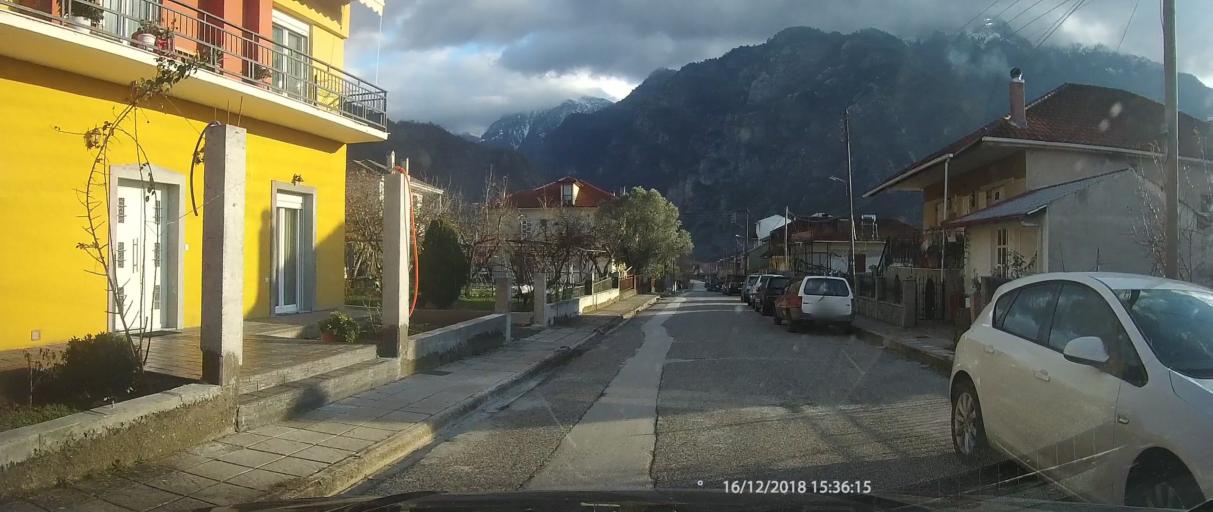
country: GR
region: Epirus
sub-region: Nomos Ioanninon
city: Konitsa
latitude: 40.0465
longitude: 20.7397
